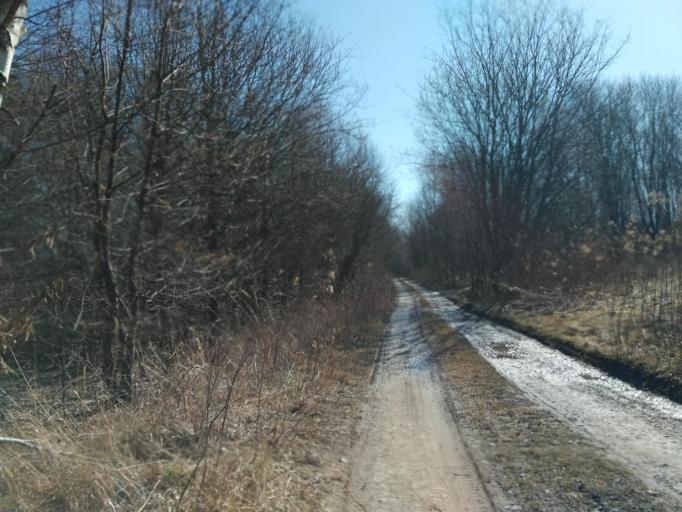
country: PL
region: Subcarpathian Voivodeship
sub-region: Powiat brzozowski
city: Blizne
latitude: 49.7615
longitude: 21.9918
